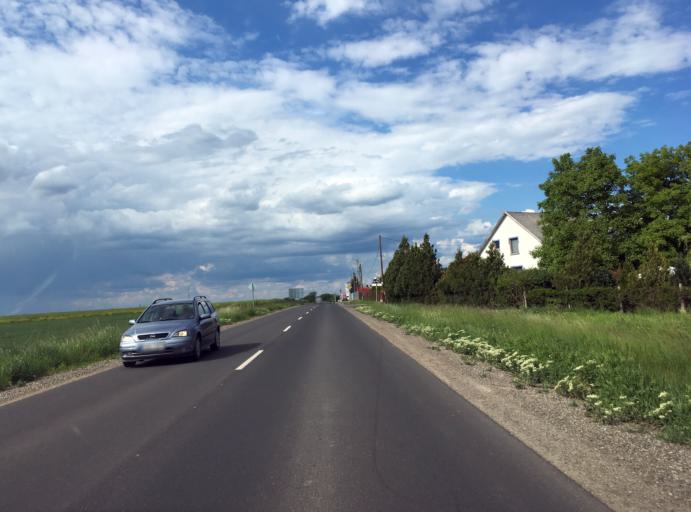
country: HU
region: Heves
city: Hered
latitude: 47.6596
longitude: 19.6193
